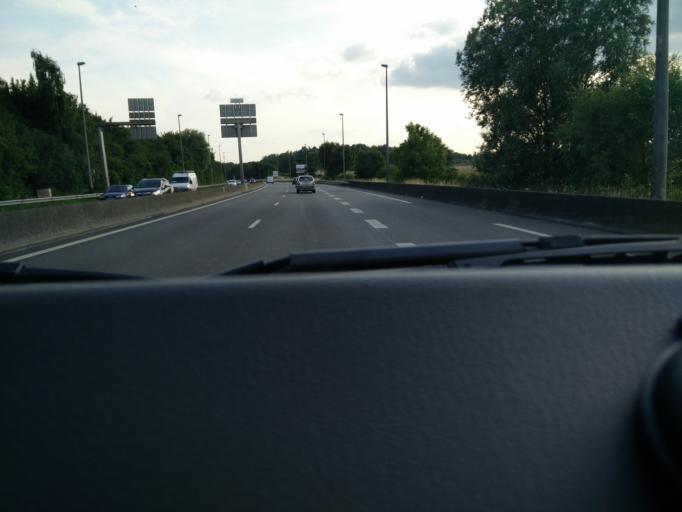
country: FR
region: Nord-Pas-de-Calais
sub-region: Departement du Nord
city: Lambersart
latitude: 50.6653
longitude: 3.0256
